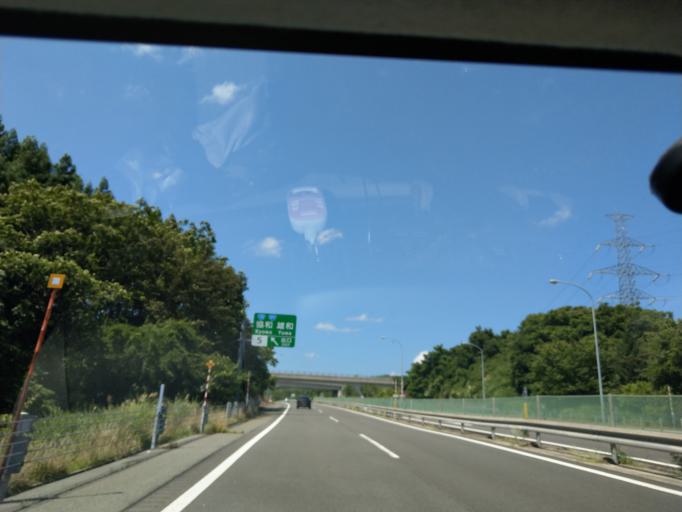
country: JP
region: Akita
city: Akita
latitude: 39.5946
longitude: 140.2843
